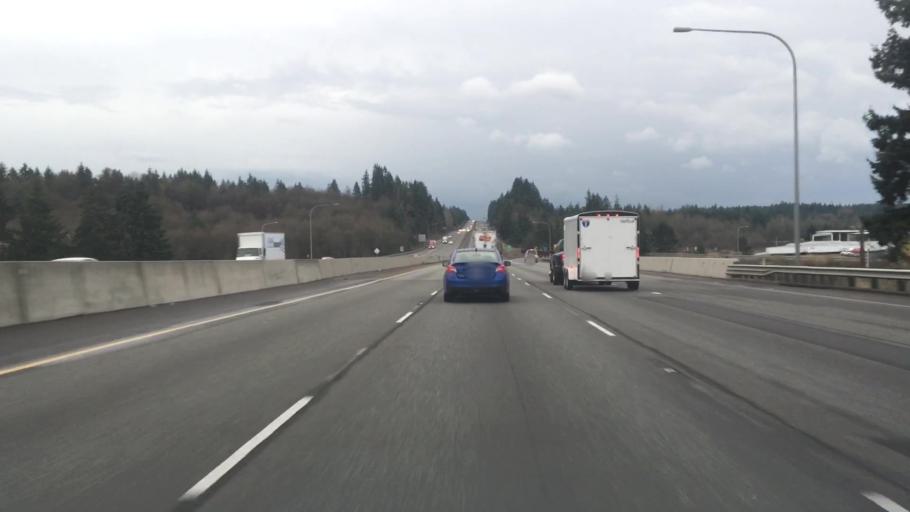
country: US
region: Washington
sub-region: Thurston County
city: Tenino
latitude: 46.8974
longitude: -122.9607
